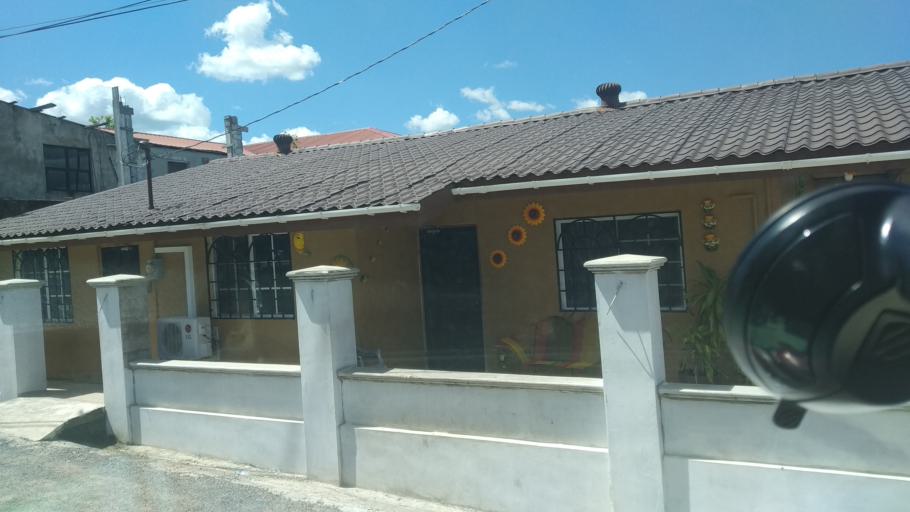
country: BZ
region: Cayo
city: Benque Viejo del Carmen
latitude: 17.0734
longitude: -89.1412
